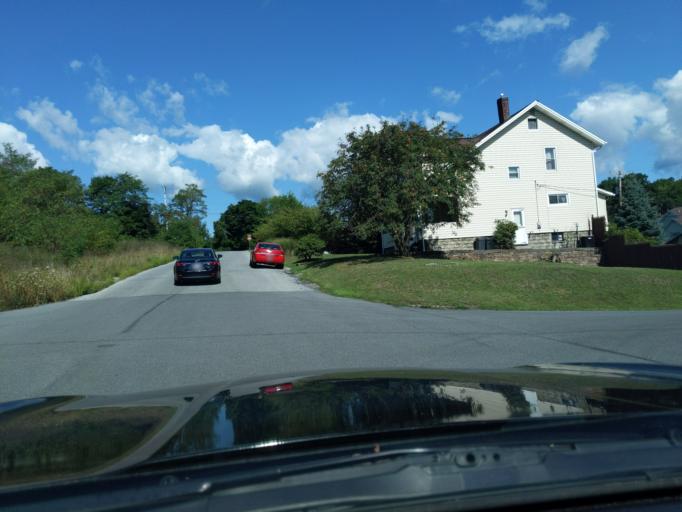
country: US
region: Pennsylvania
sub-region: Blair County
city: Altoona
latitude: 40.5381
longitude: -78.3921
